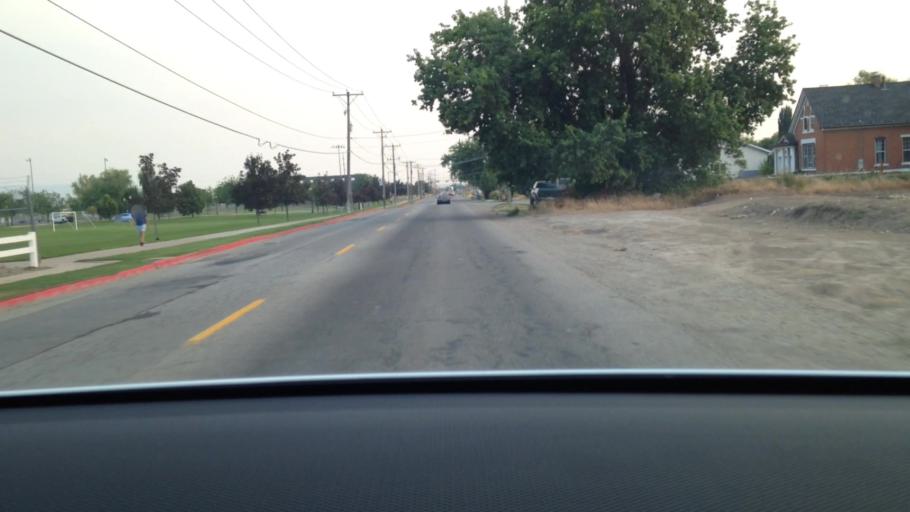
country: US
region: Utah
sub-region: Davis County
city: Layton
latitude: 41.0715
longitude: -112.0070
